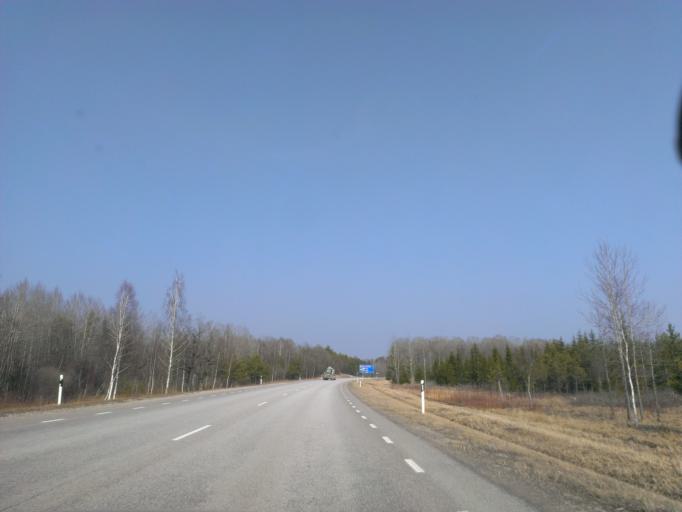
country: EE
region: Saare
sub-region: Orissaare vald
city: Orissaare
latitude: 58.4680
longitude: 22.8152
